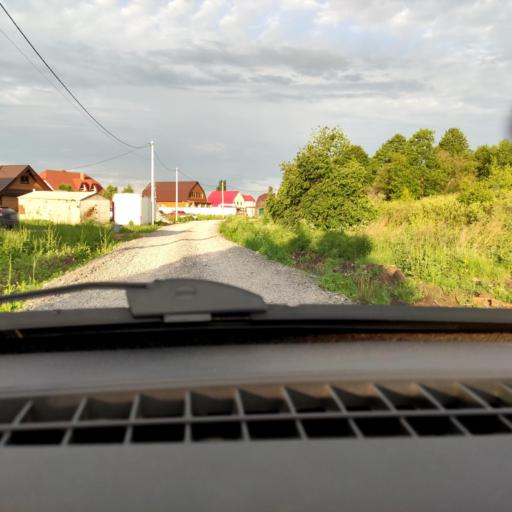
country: RU
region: Bashkortostan
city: Mikhaylovka
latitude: 54.7386
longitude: 55.8252
